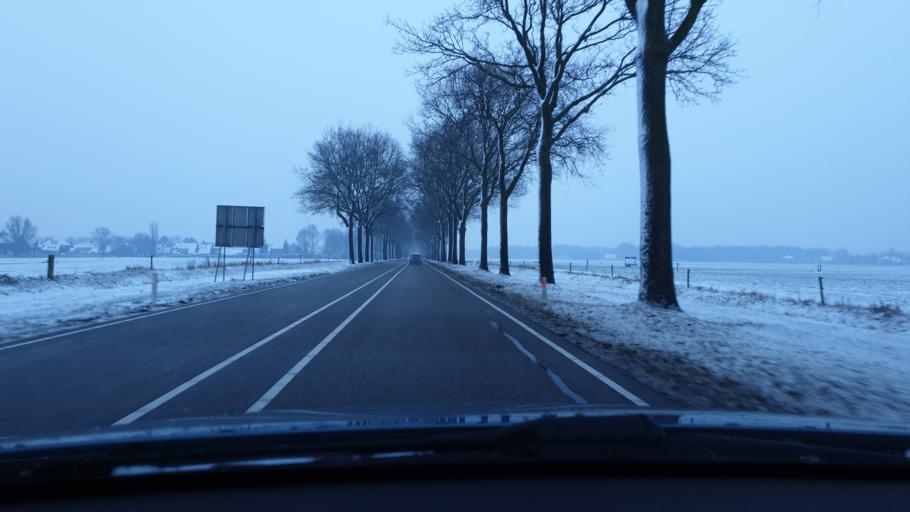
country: NL
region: North Brabant
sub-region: Gemeente Landerd
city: Zeeland
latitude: 51.7042
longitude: 5.6677
